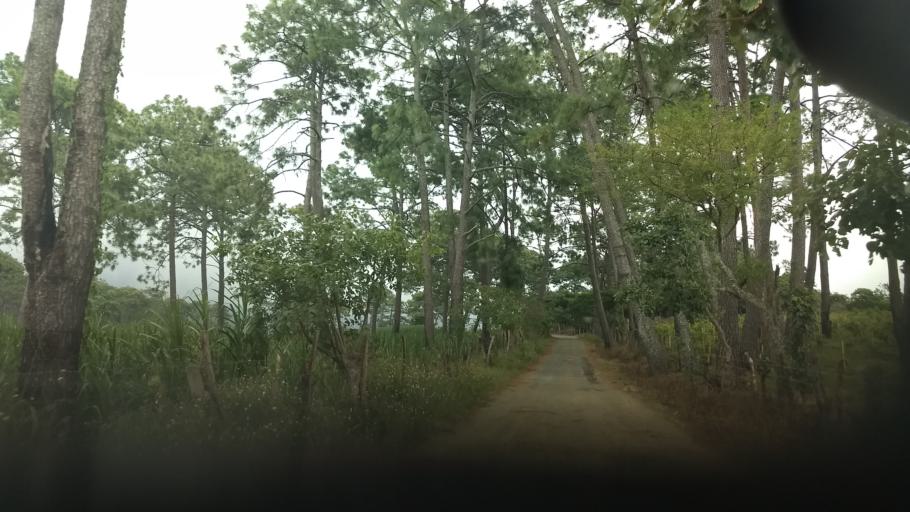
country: MX
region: Colima
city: Cofradia
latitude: 19.4692
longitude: -103.5397
